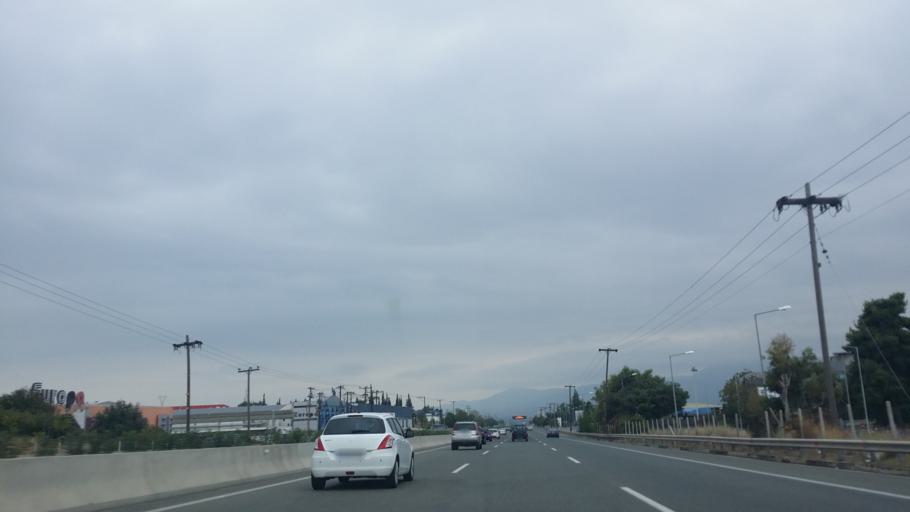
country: GR
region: Central Greece
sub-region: Nomos Voiotias
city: Oinofyta
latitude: 38.3197
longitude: 23.6230
